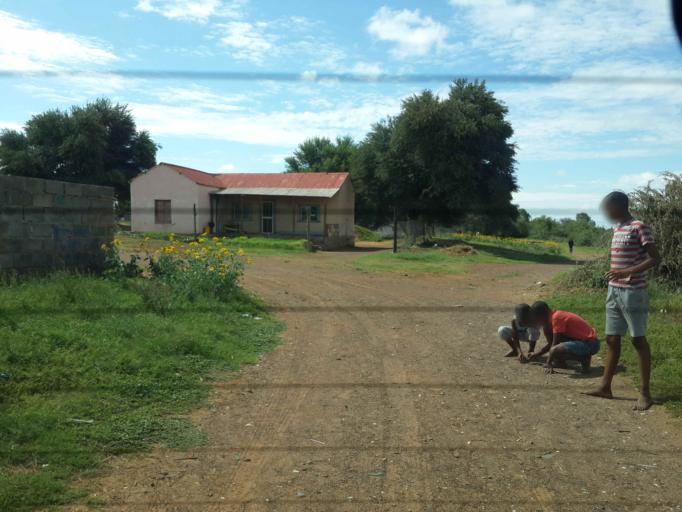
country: ZA
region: Northern Cape
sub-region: Siyanda District Municipality
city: Danielskuil
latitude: -28.1901
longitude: 23.5433
